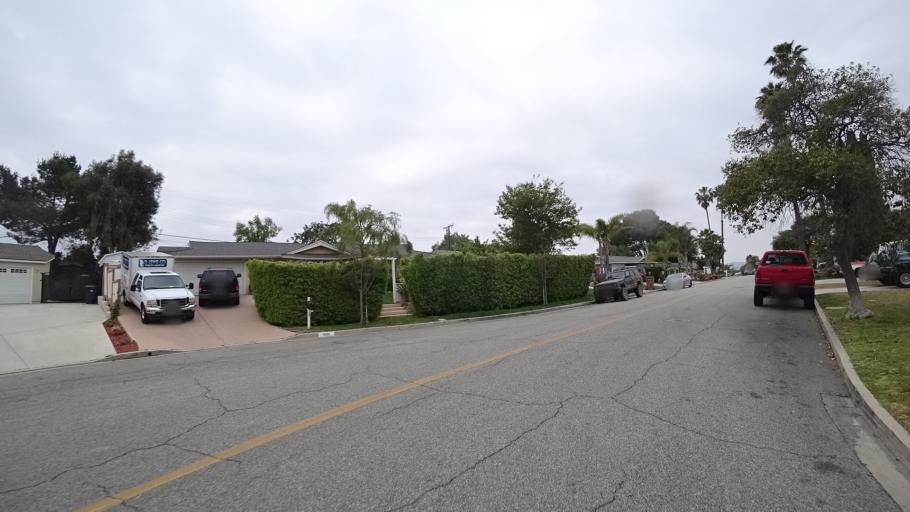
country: US
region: California
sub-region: Ventura County
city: Thousand Oaks
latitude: 34.2085
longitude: -118.8596
